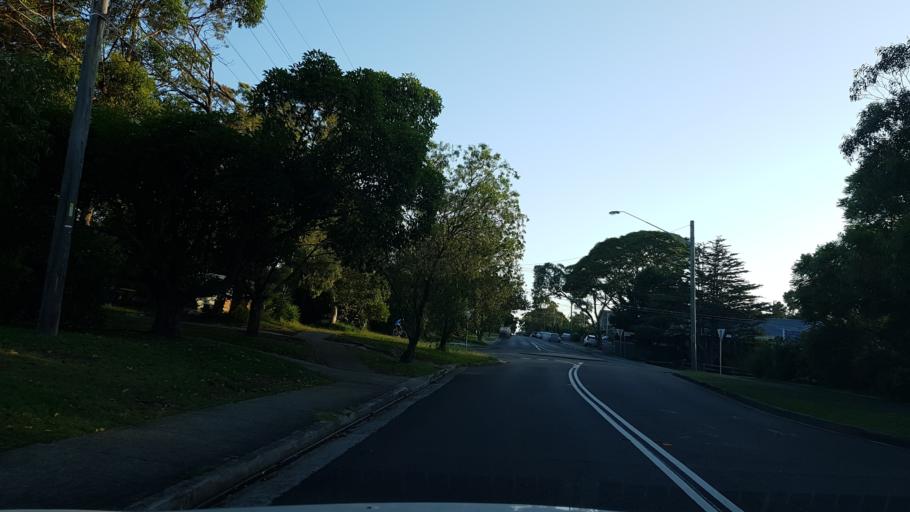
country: AU
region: New South Wales
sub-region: Warringah
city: Narrabeen
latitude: -33.7242
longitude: 151.2872
